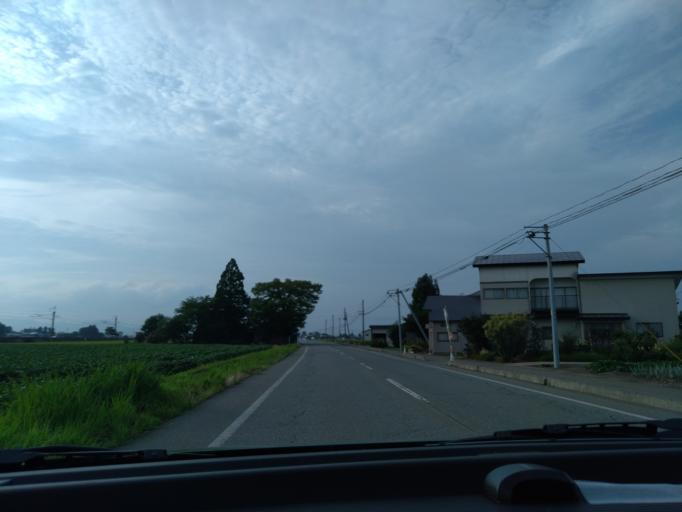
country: JP
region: Akita
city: Omagari
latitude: 39.3911
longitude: 140.5248
